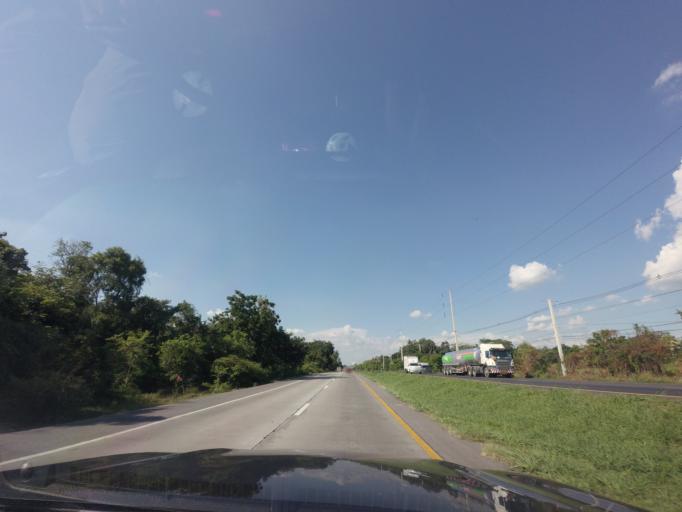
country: TH
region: Nakhon Ratchasima
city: Sida
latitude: 15.5623
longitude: 102.5517
